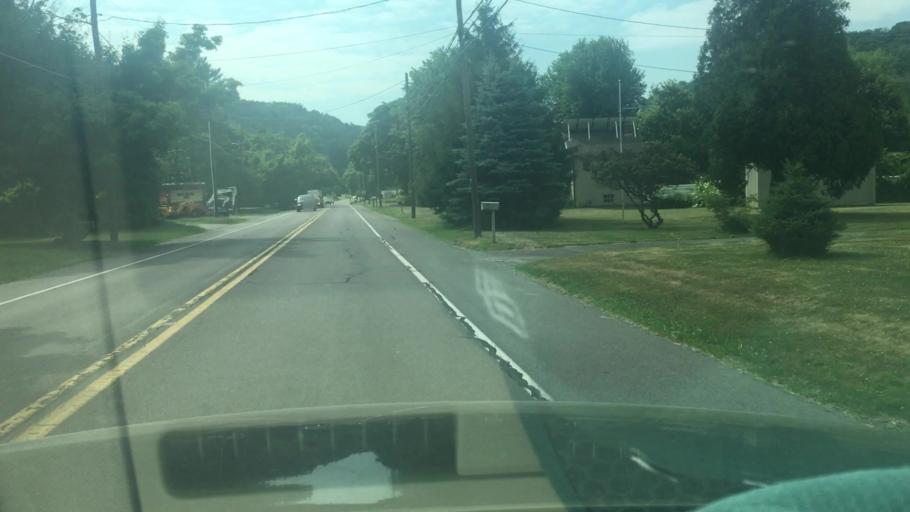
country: US
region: Pennsylvania
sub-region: Northumberland County
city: Elysburg
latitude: 40.8573
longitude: -76.5451
